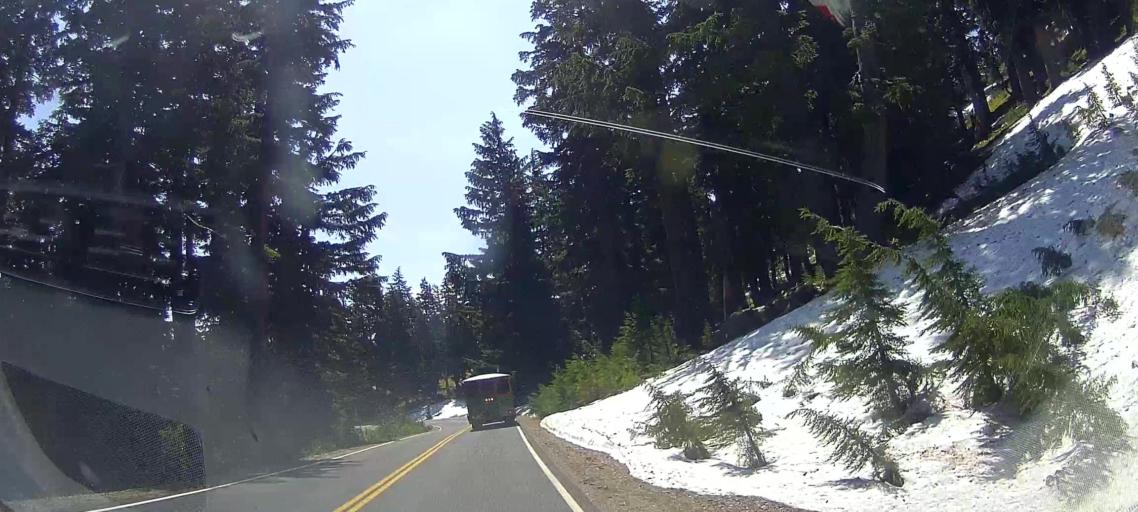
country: US
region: Oregon
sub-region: Jackson County
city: Shady Cove
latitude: 42.9807
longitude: -122.1221
